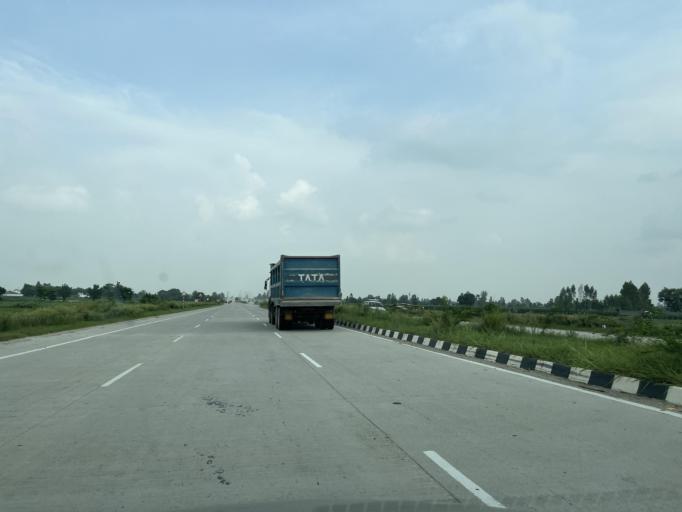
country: IN
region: Uttarakhand
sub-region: Udham Singh Nagar
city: Bazpur
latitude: 29.1479
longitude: 79.0467
